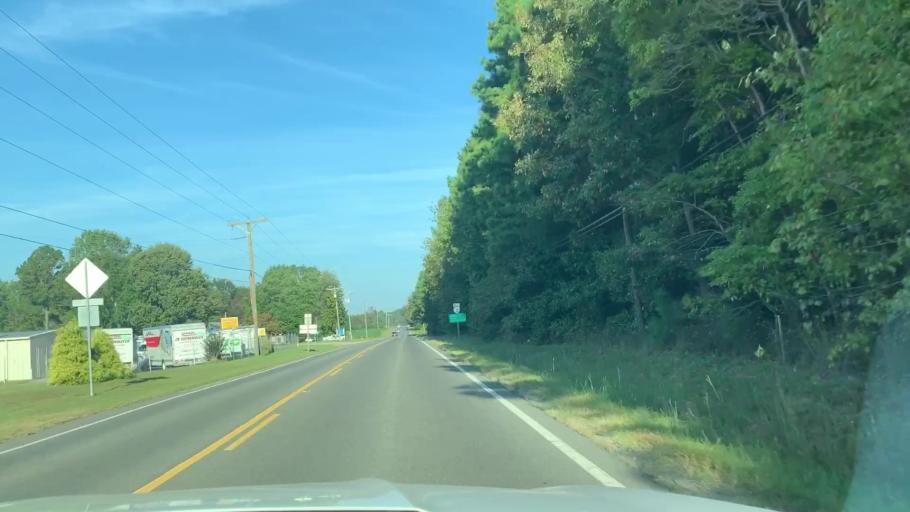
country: US
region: Virginia
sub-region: Lancaster County
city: Lancaster
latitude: 37.7646
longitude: -76.4262
